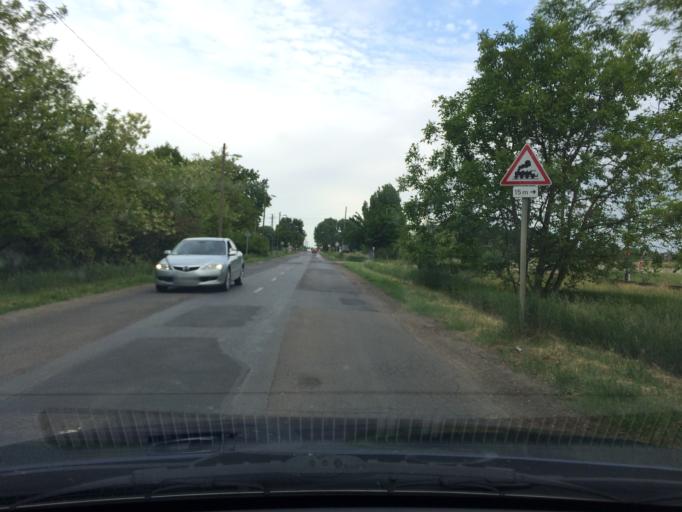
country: HU
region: Hajdu-Bihar
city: Hajdunanas
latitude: 47.9085
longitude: 21.4021
